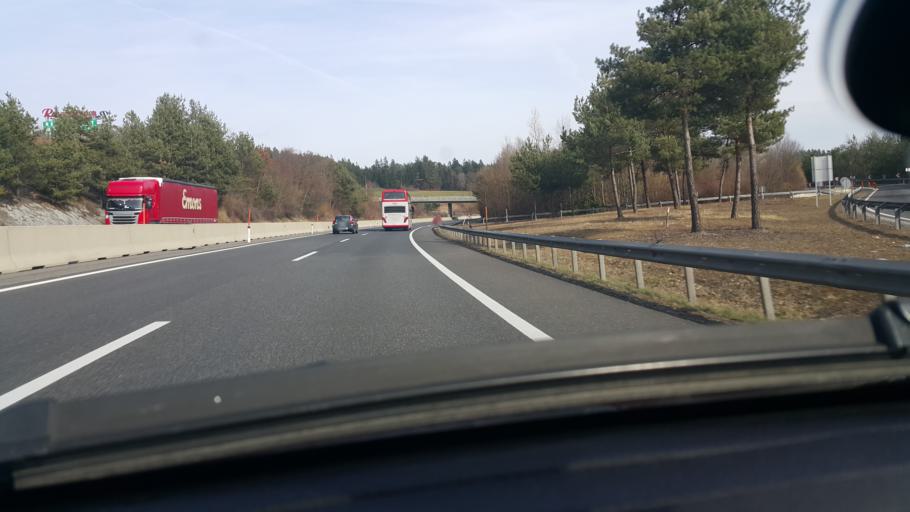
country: AT
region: Carinthia
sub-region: Politischer Bezirk Volkermarkt
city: Voelkermarkt
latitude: 46.6786
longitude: 14.5960
